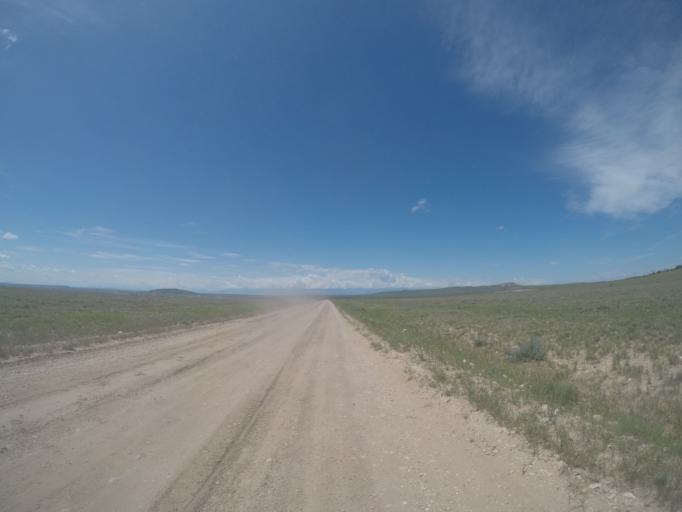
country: US
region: Montana
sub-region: Yellowstone County
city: Laurel
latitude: 45.2355
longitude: -108.6851
